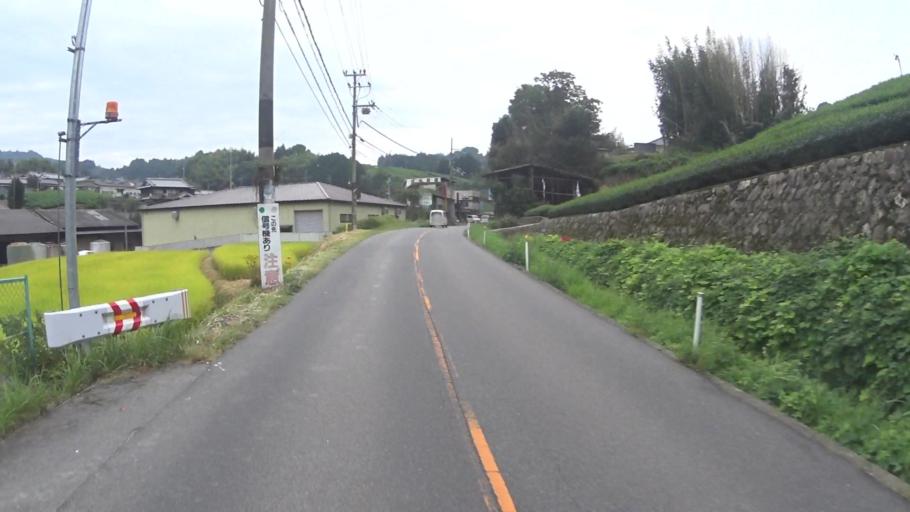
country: JP
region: Nara
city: Nara-shi
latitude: 34.7796
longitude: 135.8799
